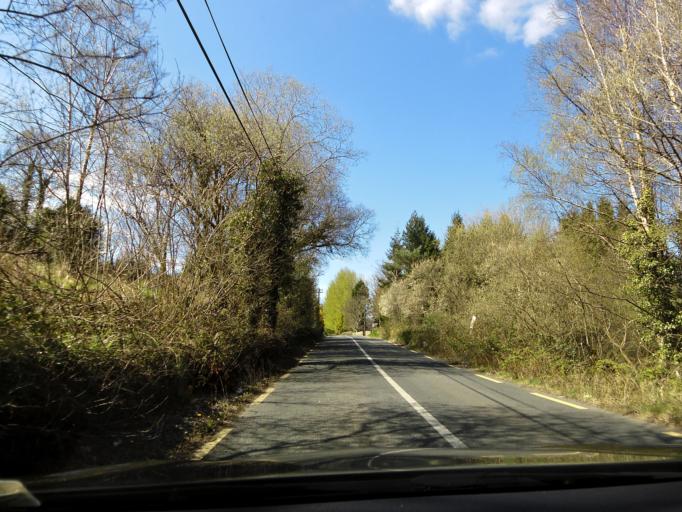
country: IE
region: Leinster
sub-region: Wicklow
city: Aughrim
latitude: 52.8509
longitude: -6.3098
